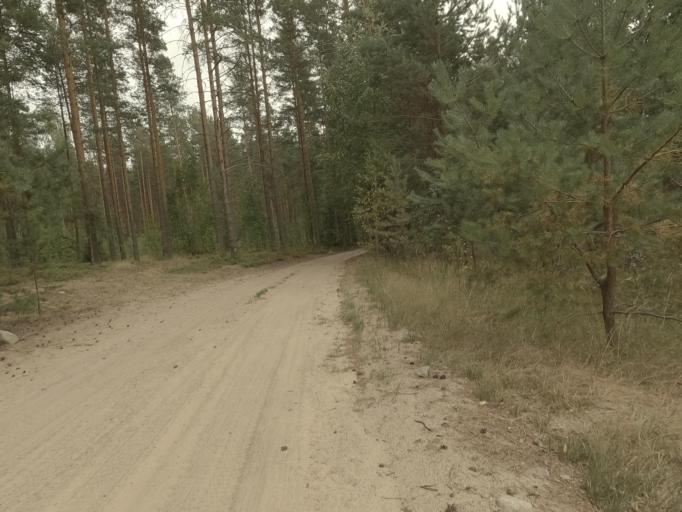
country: RU
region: Leningrad
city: Kamennogorsk
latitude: 60.9996
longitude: 29.1823
